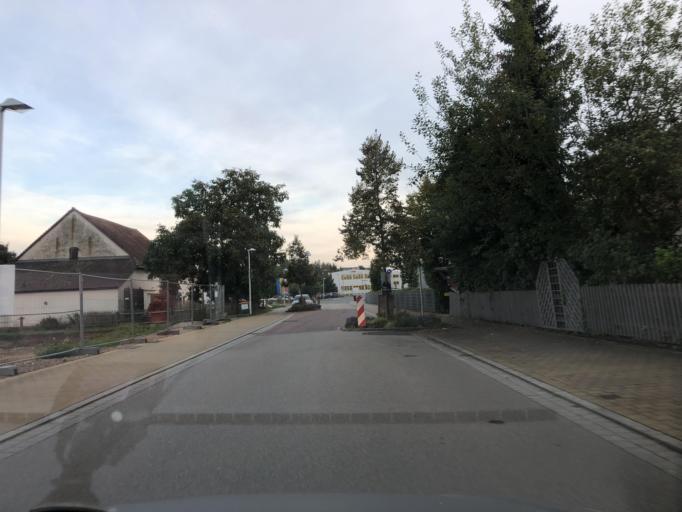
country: DE
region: Bavaria
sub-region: Regierungsbezirk Mittelfranken
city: Zirndorf
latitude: 49.4336
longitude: 10.9335
